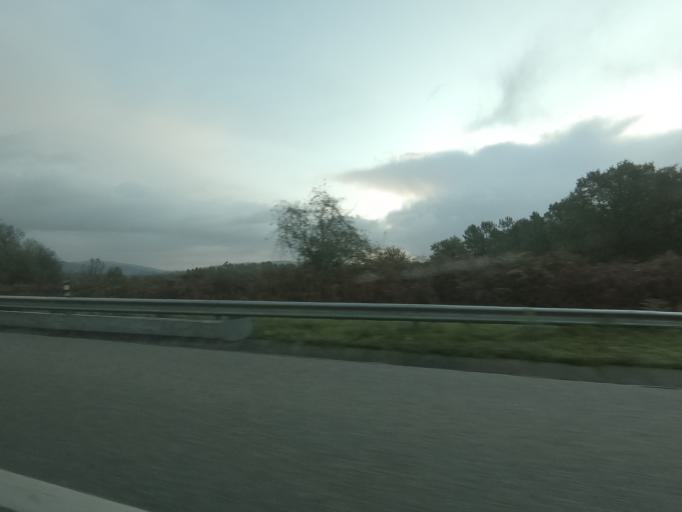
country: PT
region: Braga
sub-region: Vila Verde
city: Prado
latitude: 41.6582
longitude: -8.5483
